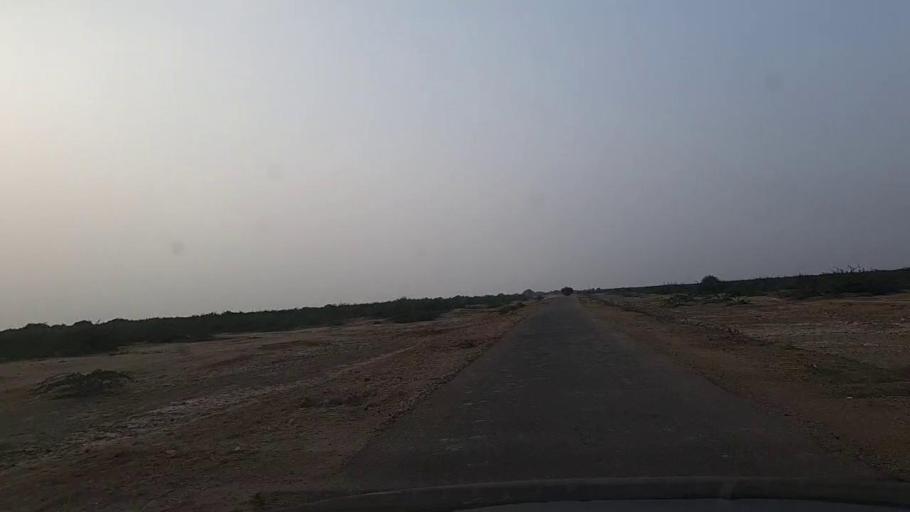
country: PK
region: Sindh
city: Gharo
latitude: 24.7813
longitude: 67.7307
